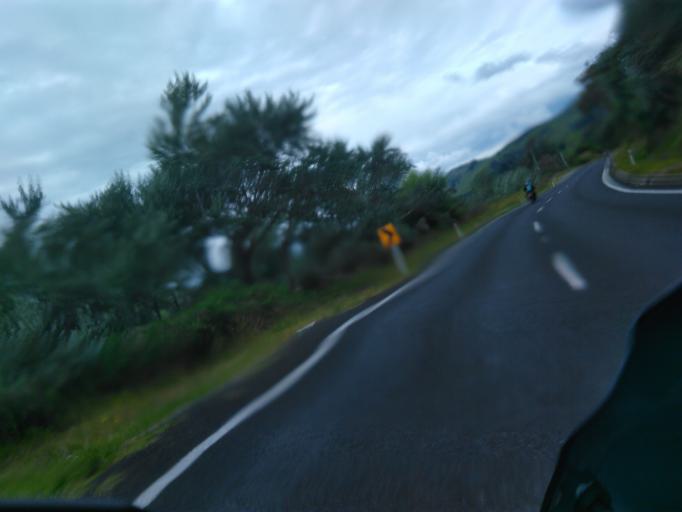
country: NZ
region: Gisborne
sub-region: Gisborne District
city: Gisborne
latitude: -38.4571
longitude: 177.6425
